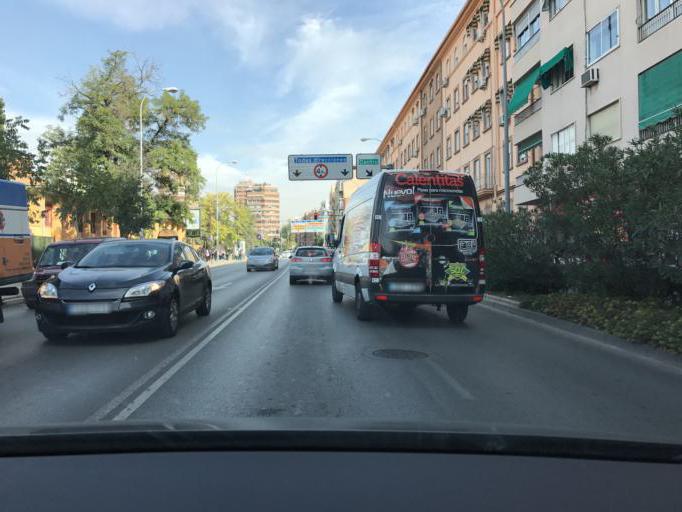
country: ES
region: Andalusia
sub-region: Provincia de Granada
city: Granada
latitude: 37.1818
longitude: -3.6059
